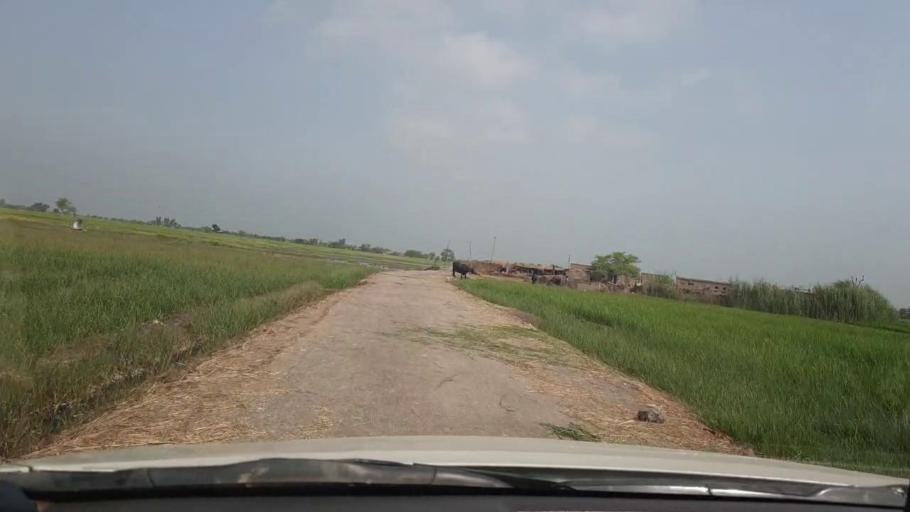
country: PK
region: Sindh
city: Shikarpur
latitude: 27.9890
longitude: 68.6079
